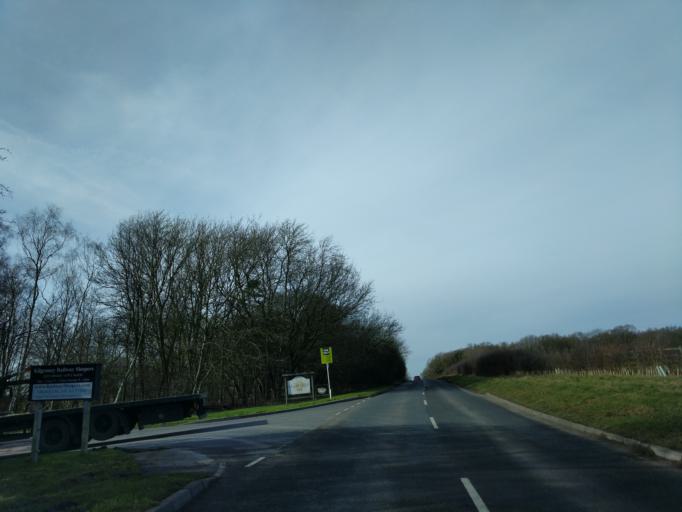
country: GB
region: England
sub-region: Nottinghamshire
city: Cotgrave
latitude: 52.8991
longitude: -1.0286
